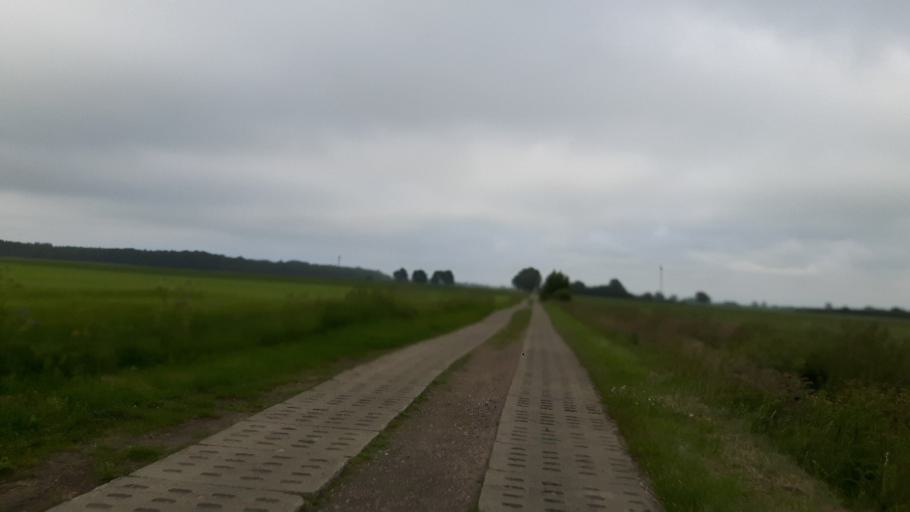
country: PL
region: West Pomeranian Voivodeship
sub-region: Powiat koszalinski
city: Sianow
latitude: 54.3027
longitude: 16.2828
